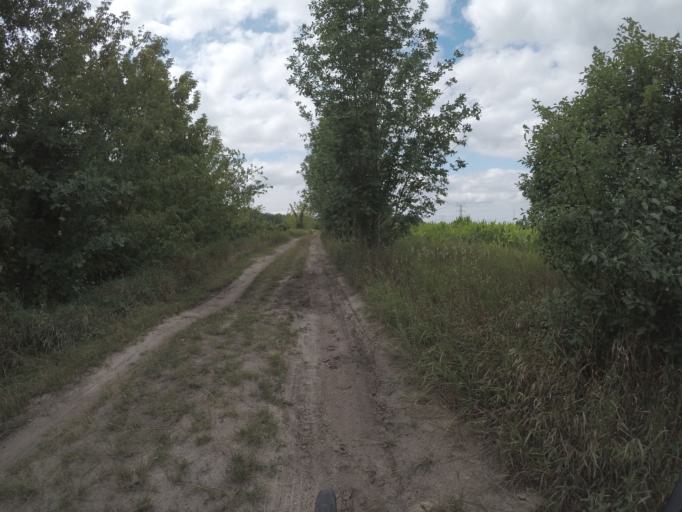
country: DE
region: Brandenburg
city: Falkensee
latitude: 52.6073
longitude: 13.0652
